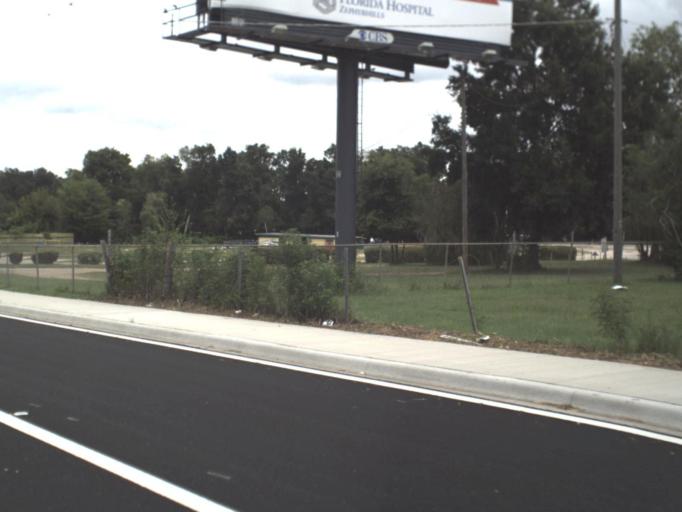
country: US
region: Florida
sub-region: Pasco County
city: Dade City North
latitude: 28.3962
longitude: -82.1955
